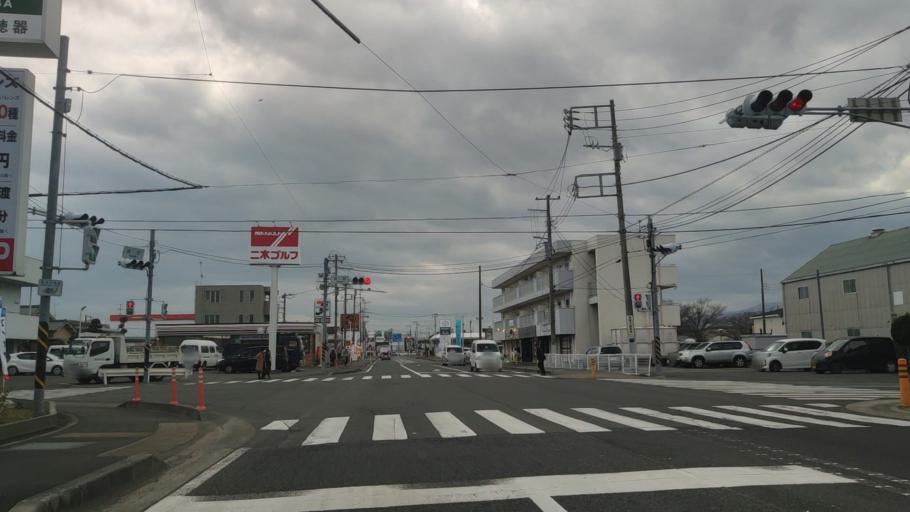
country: JP
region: Kanagawa
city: Odawara
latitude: 35.2927
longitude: 139.1676
